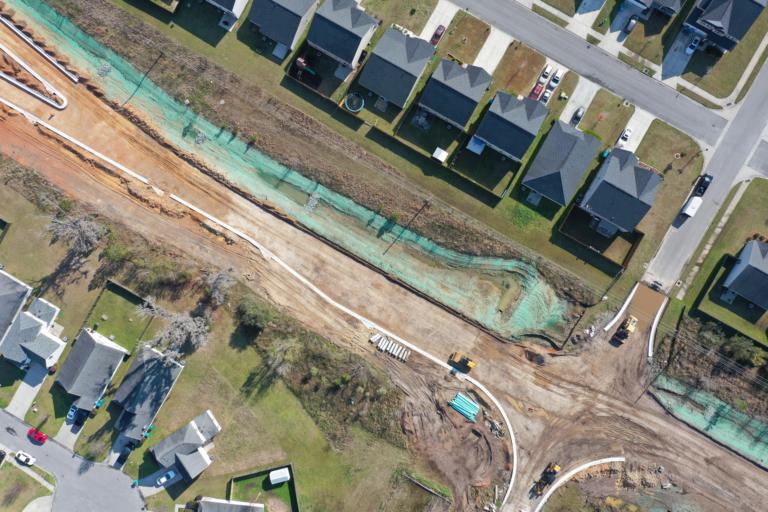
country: US
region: Georgia
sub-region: Chatham County
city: Port Wentworth
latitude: 32.1838
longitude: -81.2216
